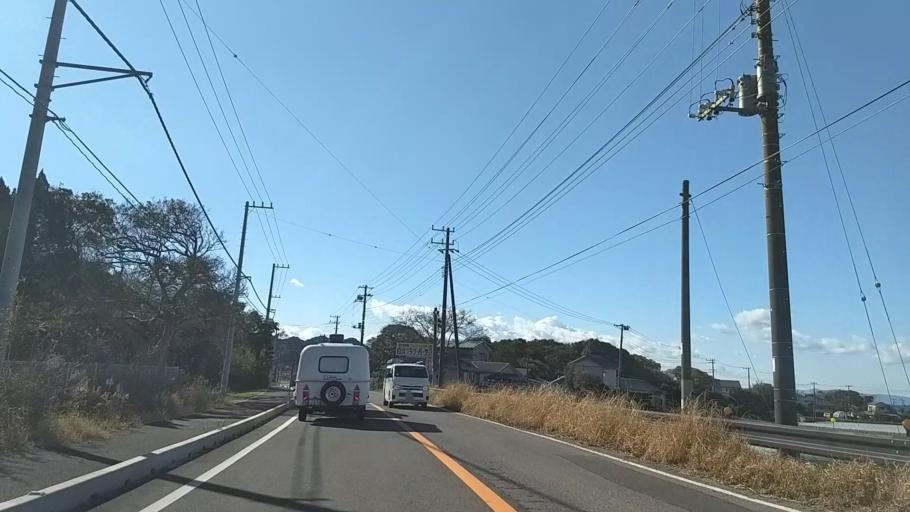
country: JP
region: Chiba
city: Tateyama
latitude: 34.9373
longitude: 139.8411
